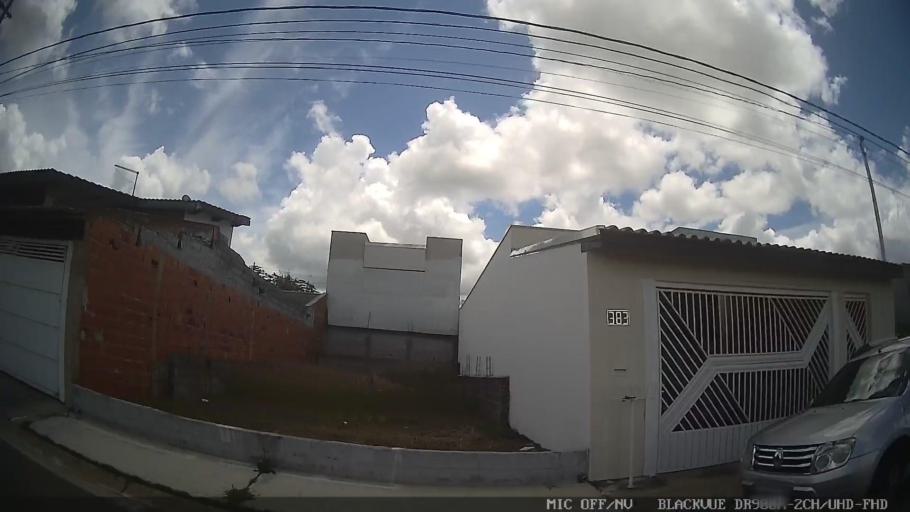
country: BR
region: Sao Paulo
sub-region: Braganca Paulista
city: Braganca Paulista
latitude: -22.9305
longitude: -46.5665
